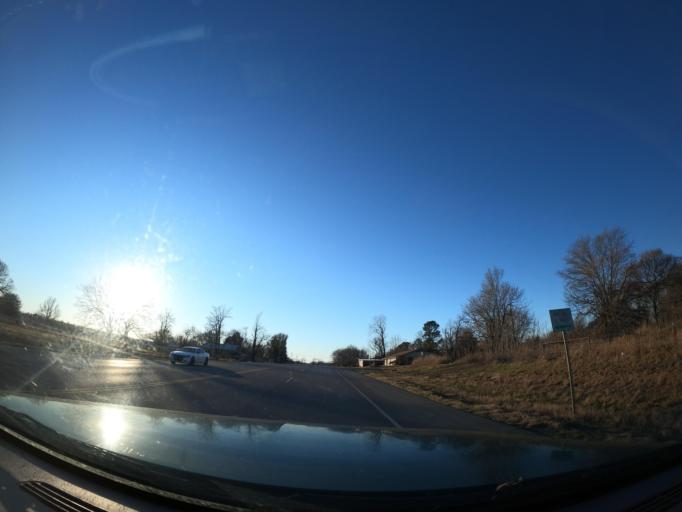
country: US
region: Oklahoma
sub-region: Pittsburg County
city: Krebs
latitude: 34.8942
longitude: -95.6468
